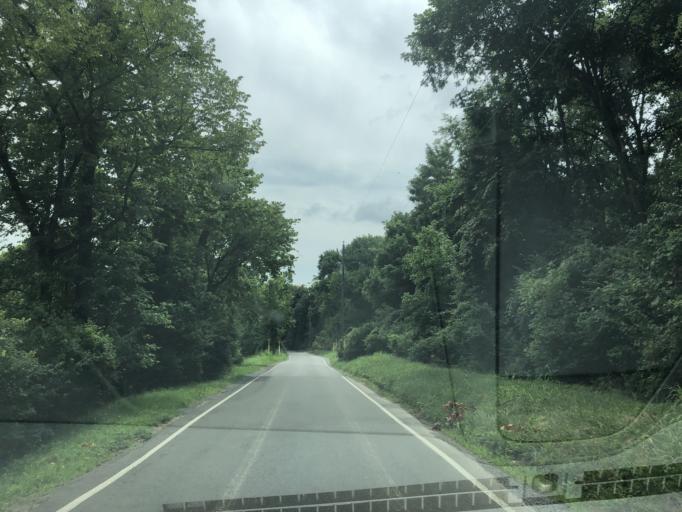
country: US
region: Tennessee
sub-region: Williamson County
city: Nolensville
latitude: 36.0091
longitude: -86.6974
